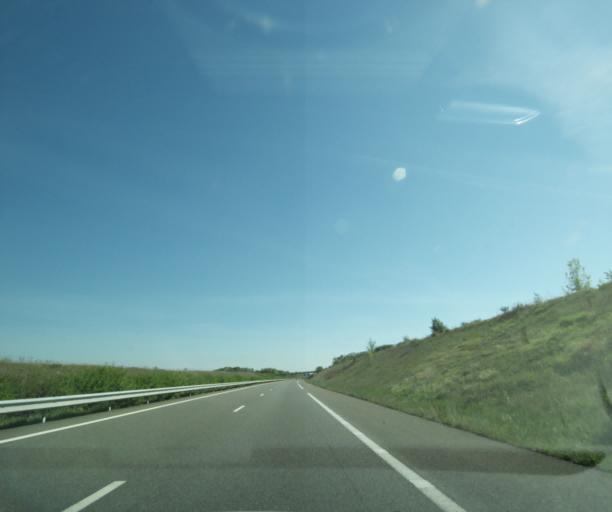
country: FR
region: Midi-Pyrenees
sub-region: Departement du Tarn-et-Garonne
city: Caussade
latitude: 44.2233
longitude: 1.5369
